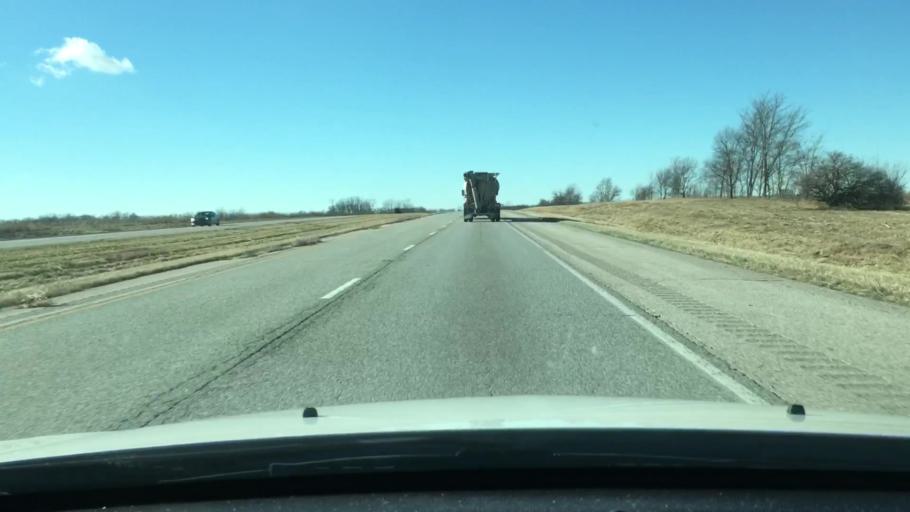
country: US
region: Illinois
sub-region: Pike County
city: Griggsville
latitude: 39.6784
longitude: -90.7050
